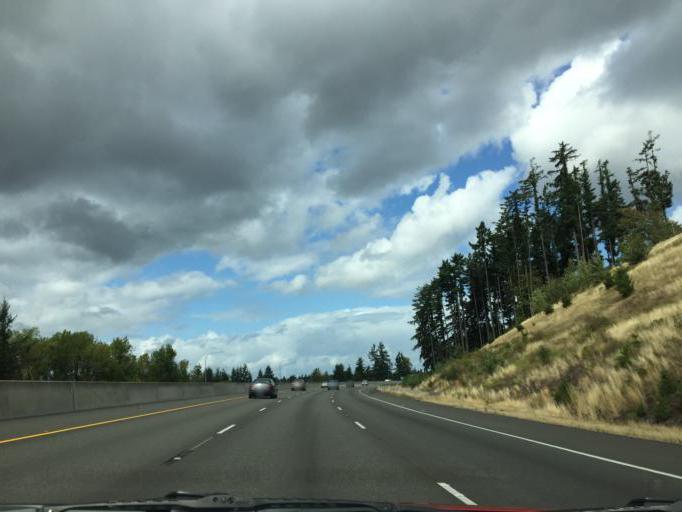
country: US
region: Washington
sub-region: Thurston County
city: Grand Mound
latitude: 46.7954
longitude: -123.0102
